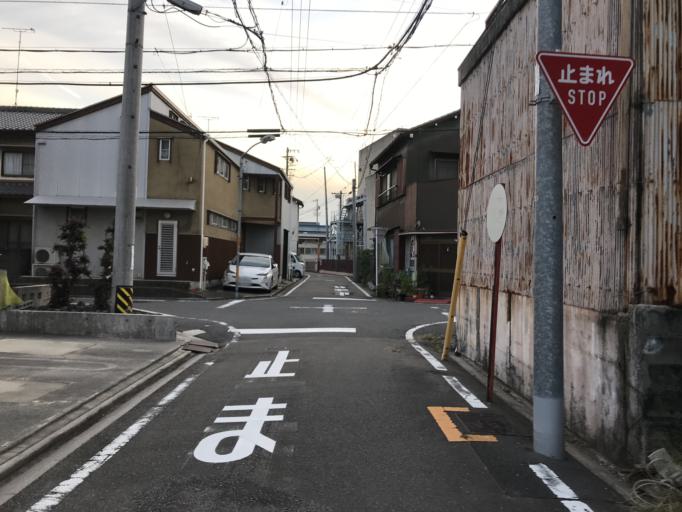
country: JP
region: Aichi
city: Nagoya-shi
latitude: 35.1934
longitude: 136.8509
